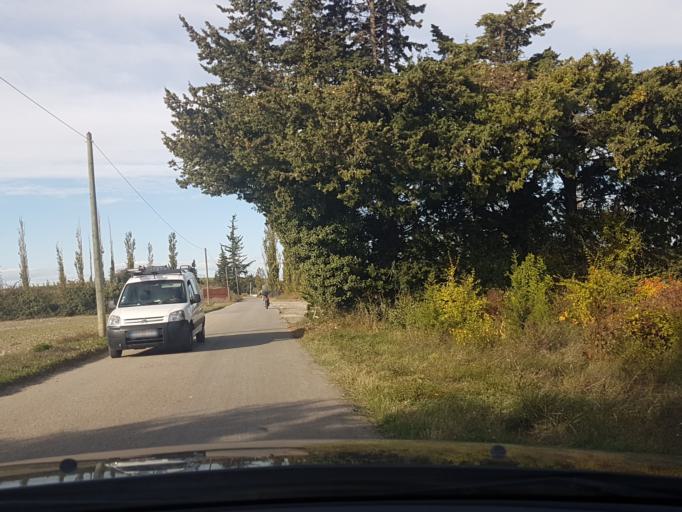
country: FR
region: Provence-Alpes-Cote d'Azur
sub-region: Departement du Vaucluse
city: Saint-Saturnin-les-Avignon
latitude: 43.9690
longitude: 4.9388
